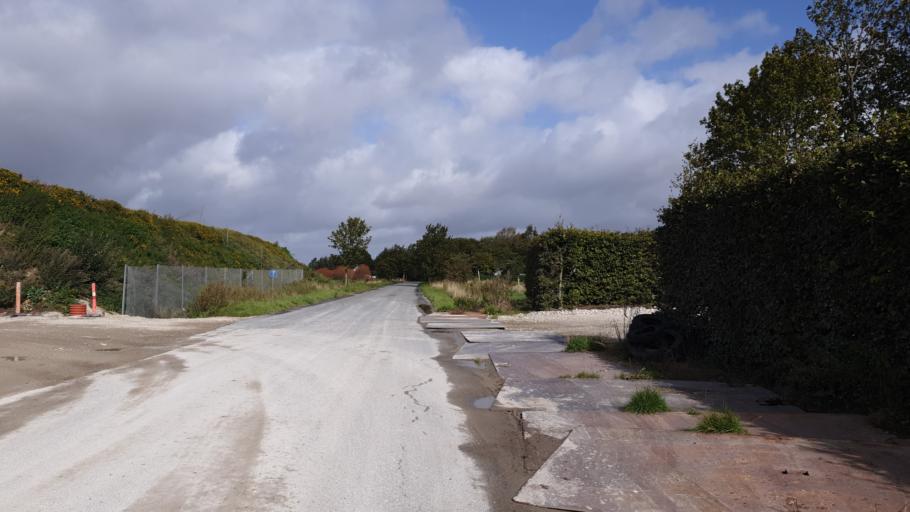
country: DK
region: Central Jutland
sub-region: Hedensted Kommune
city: Hedensted
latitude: 55.8130
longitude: 9.6854
